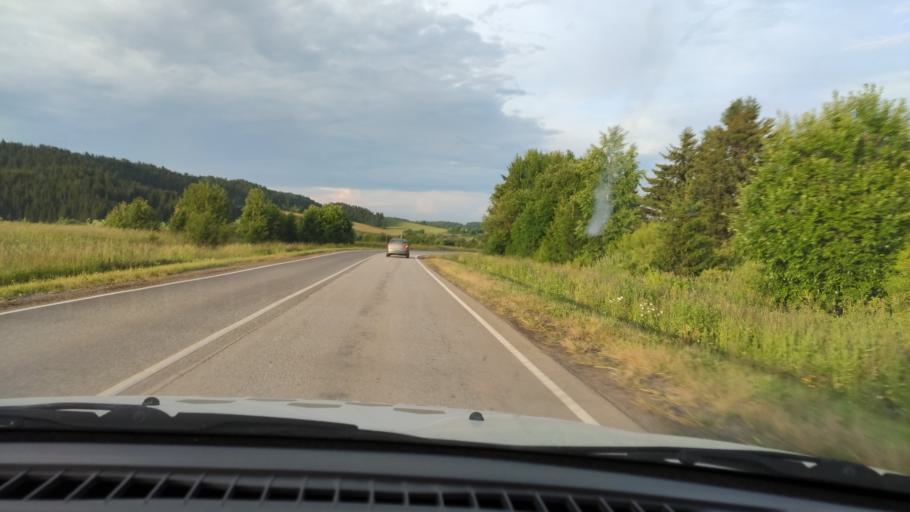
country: RU
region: Perm
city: Kukushtan
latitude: 57.4353
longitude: 56.3754
